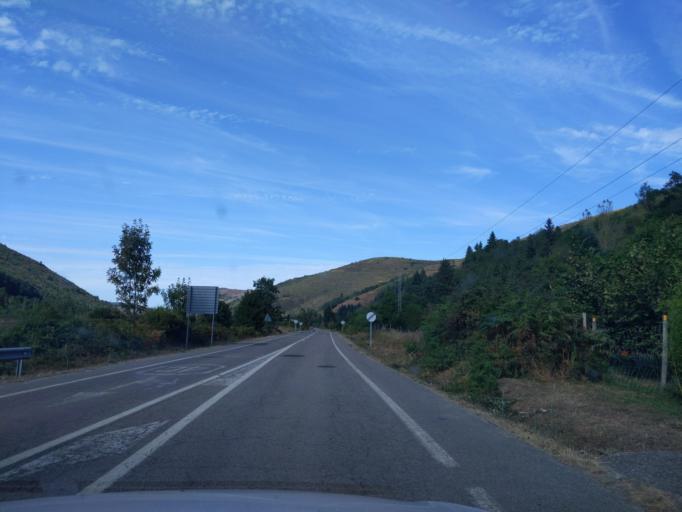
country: ES
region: La Rioja
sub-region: Provincia de La Rioja
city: Ezcaray
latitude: 42.3057
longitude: -3.0211
